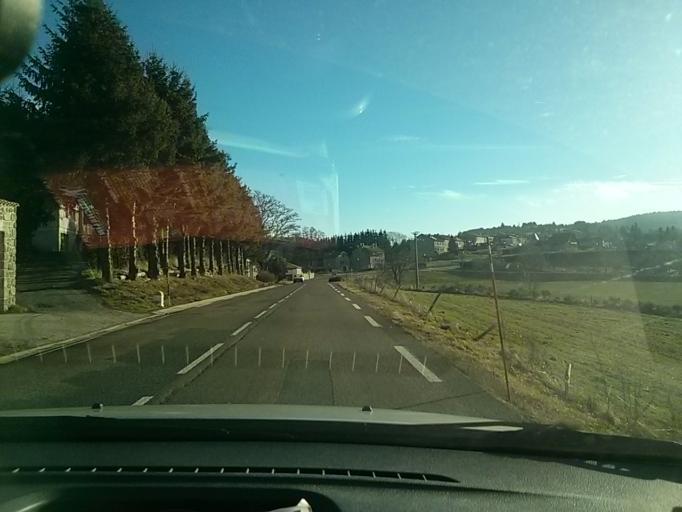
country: FR
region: Rhone-Alpes
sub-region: Departement de la Loire
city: Bourg-Argental
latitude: 45.3711
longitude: 4.5097
